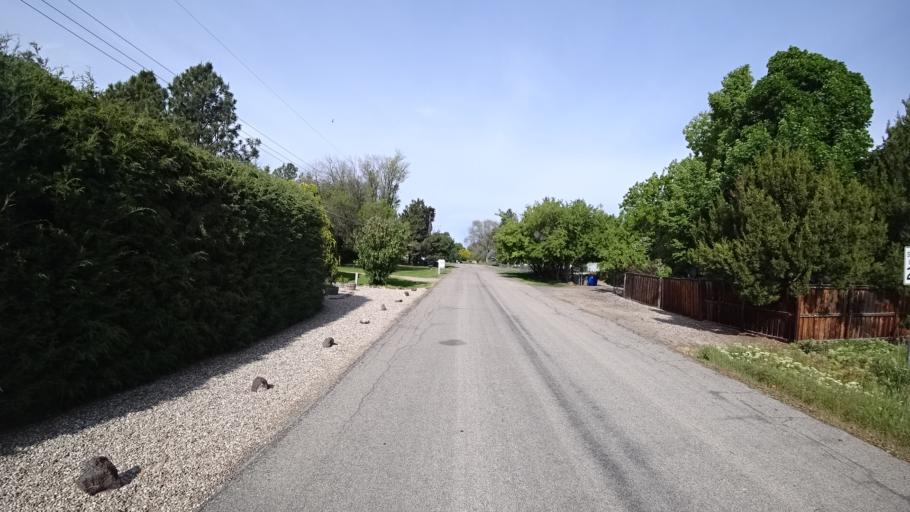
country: US
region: Idaho
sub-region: Ada County
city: Garden City
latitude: 43.5654
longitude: -116.2952
